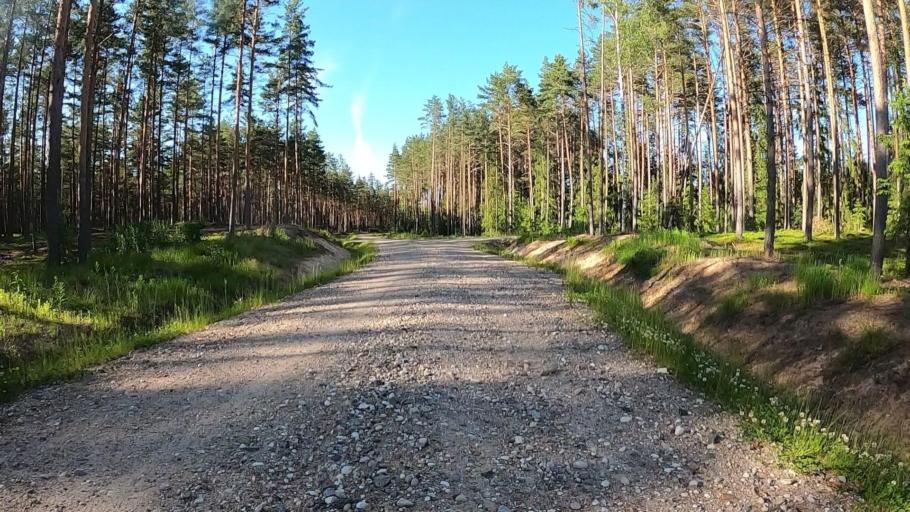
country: LV
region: Carnikava
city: Carnikava
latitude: 57.1089
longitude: 24.2526
